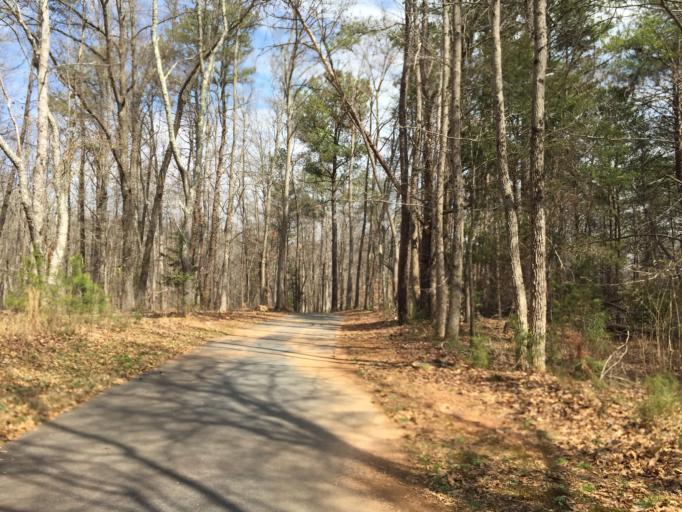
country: US
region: South Carolina
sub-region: Greenville County
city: Mauldin
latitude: 34.7867
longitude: -82.3652
